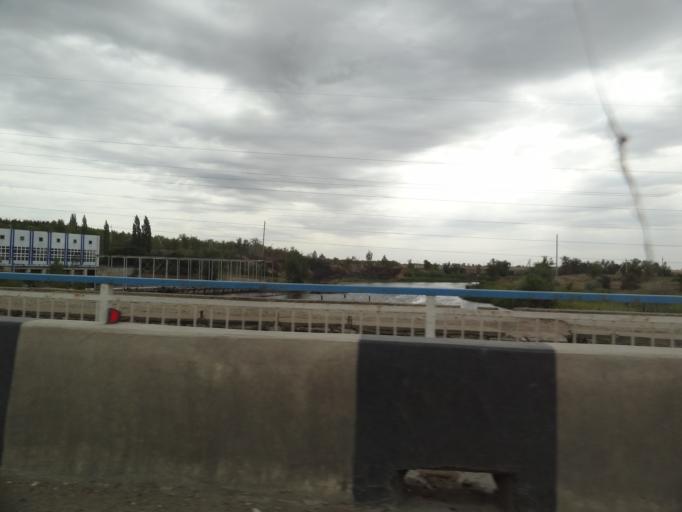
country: RU
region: Saratov
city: Shumeyka
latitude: 51.5215
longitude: 46.2582
